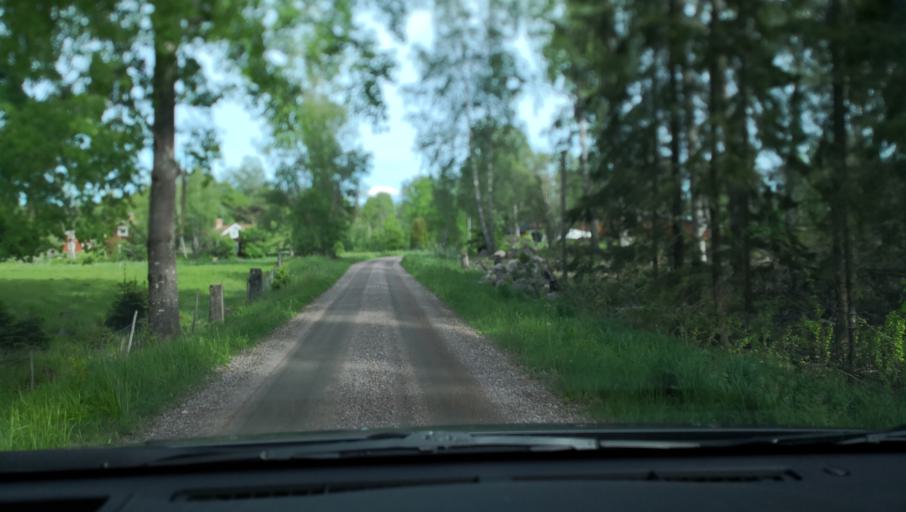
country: SE
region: Vaestmanland
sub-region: Kungsors Kommun
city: Kungsoer
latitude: 59.3632
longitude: 16.0209
